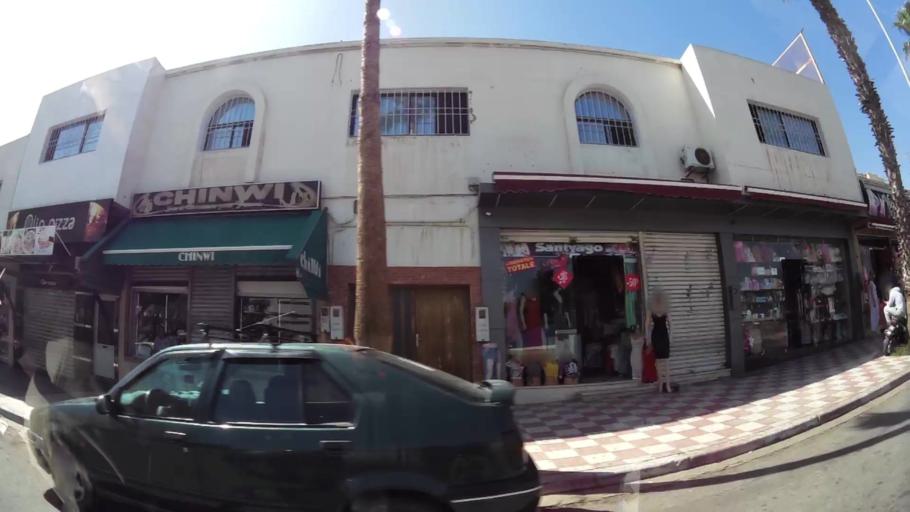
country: MA
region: Souss-Massa-Draa
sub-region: Agadir-Ida-ou-Tnan
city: Agadir
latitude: 30.4203
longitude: -9.5952
